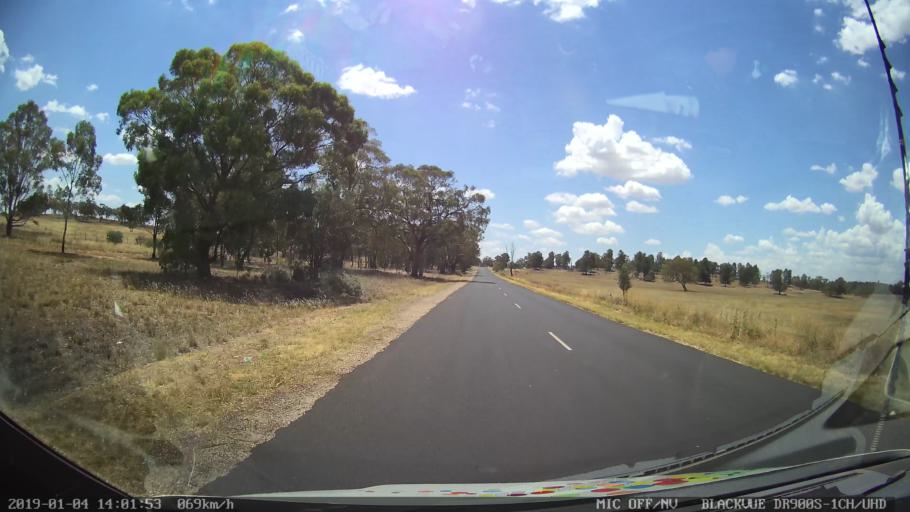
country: AU
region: New South Wales
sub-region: Dubbo Municipality
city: Dubbo
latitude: -32.2920
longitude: 148.5986
